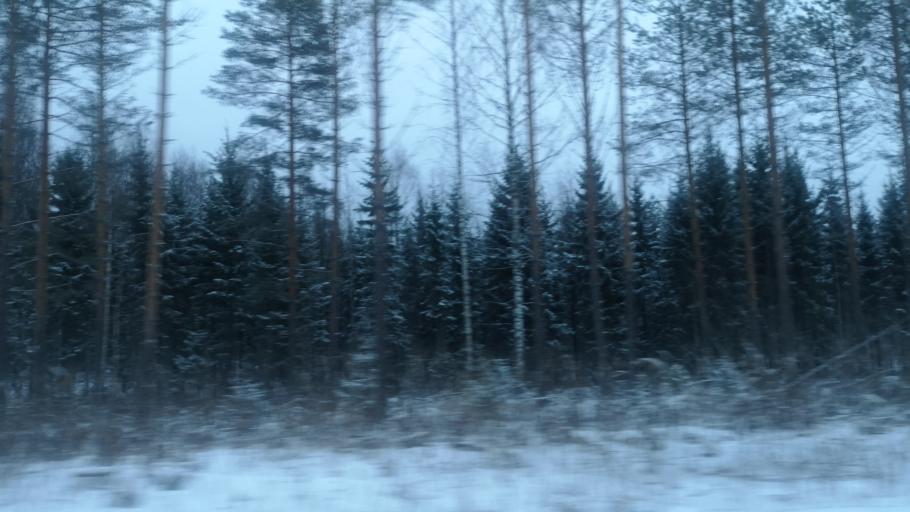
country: FI
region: Southern Savonia
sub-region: Savonlinna
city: Enonkoski
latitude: 62.0940
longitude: 28.6699
